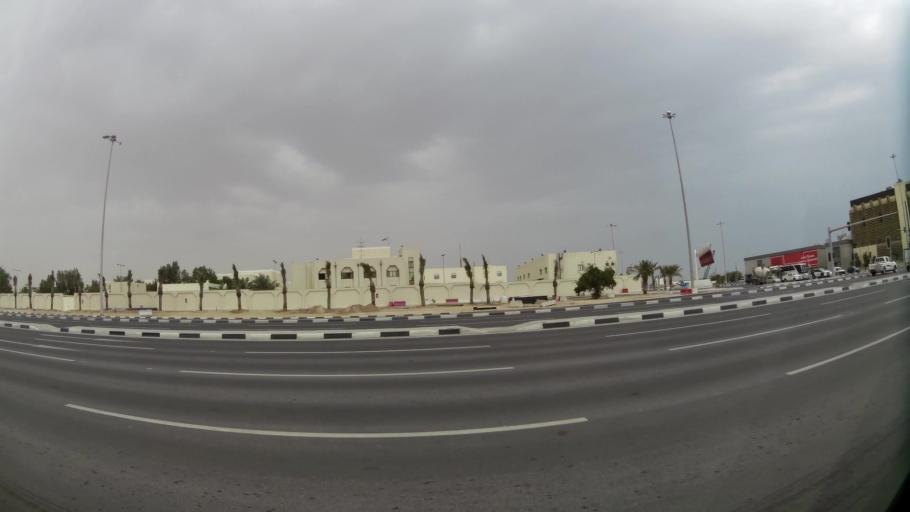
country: QA
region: Baladiyat ad Dawhah
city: Doha
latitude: 25.3014
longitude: 51.5066
